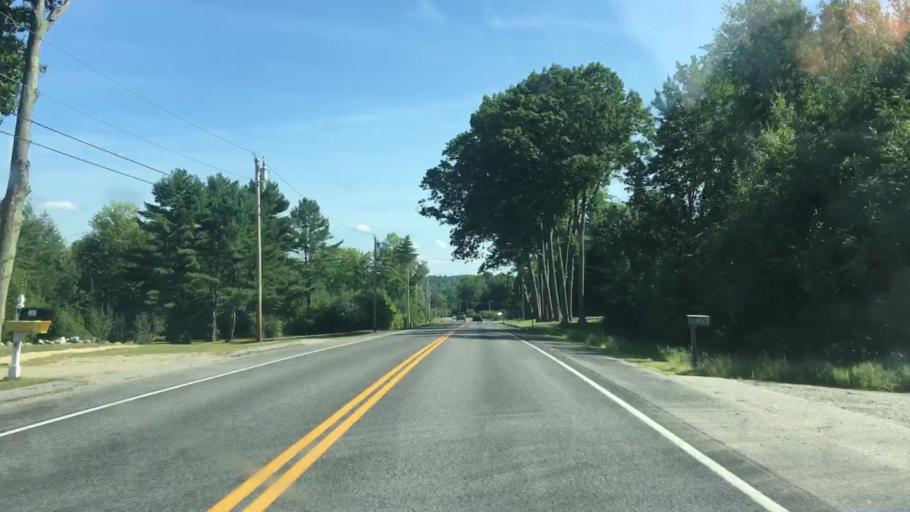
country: US
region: Maine
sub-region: Androscoggin County
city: Lisbon
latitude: 44.0544
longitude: -70.0845
